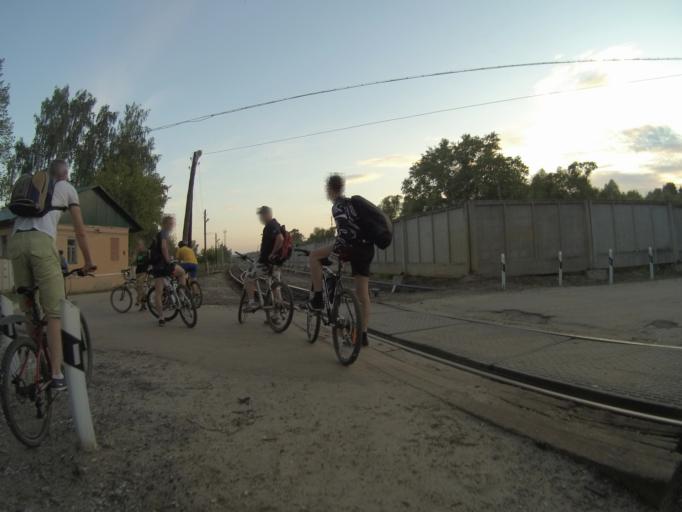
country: RU
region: Vladimir
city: Vladimir
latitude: 56.1191
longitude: 40.4006
